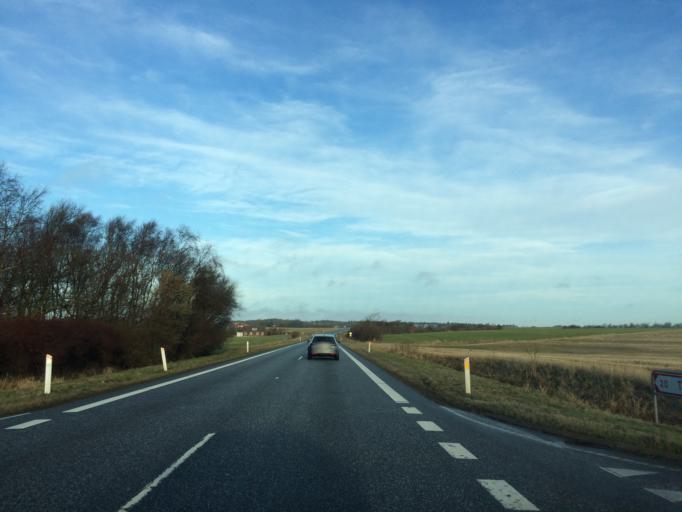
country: DK
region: North Denmark
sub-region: Thisted Kommune
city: Hurup
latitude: 56.8203
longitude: 8.4929
